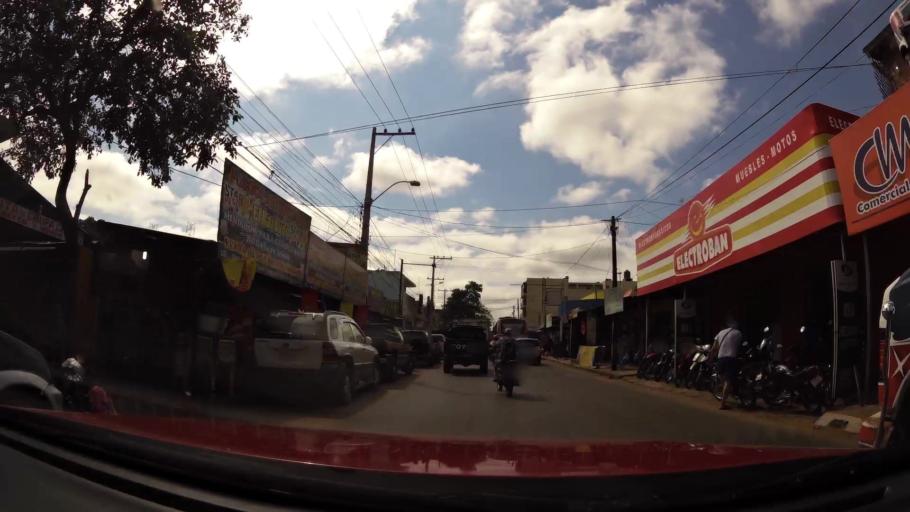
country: PY
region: Central
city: San Lorenzo
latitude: -25.2720
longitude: -57.4903
